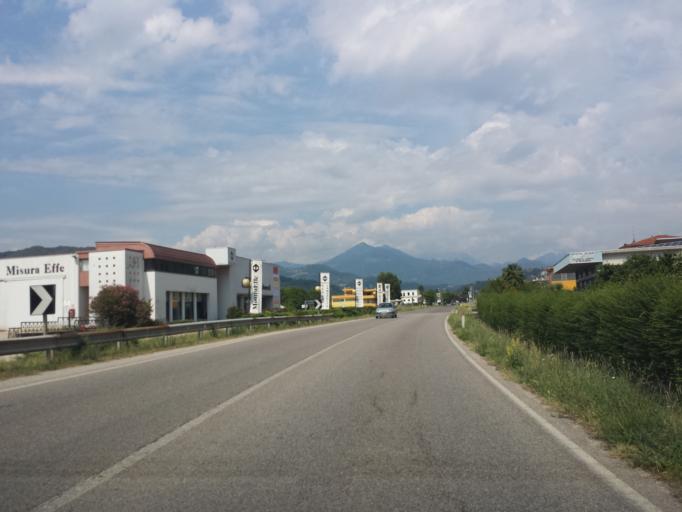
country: IT
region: Veneto
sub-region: Provincia di Vicenza
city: Cereda-Cozza Cornedo
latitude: 45.6017
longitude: 11.3579
